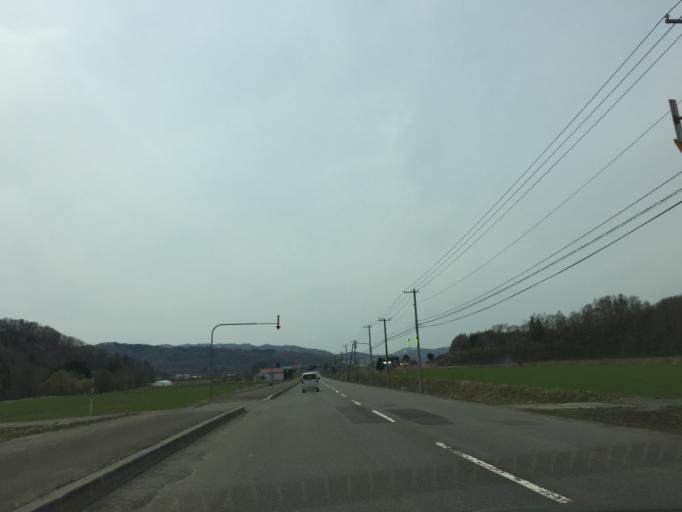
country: JP
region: Hokkaido
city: Ashibetsu
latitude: 43.5492
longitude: 142.1728
